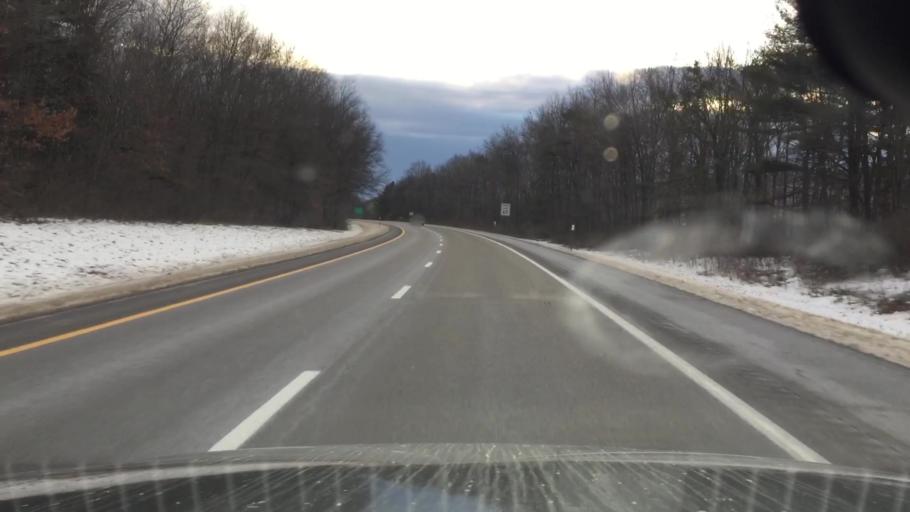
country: US
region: Pennsylvania
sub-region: Bradford County
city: South Waverly
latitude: 42.0012
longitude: -76.6186
